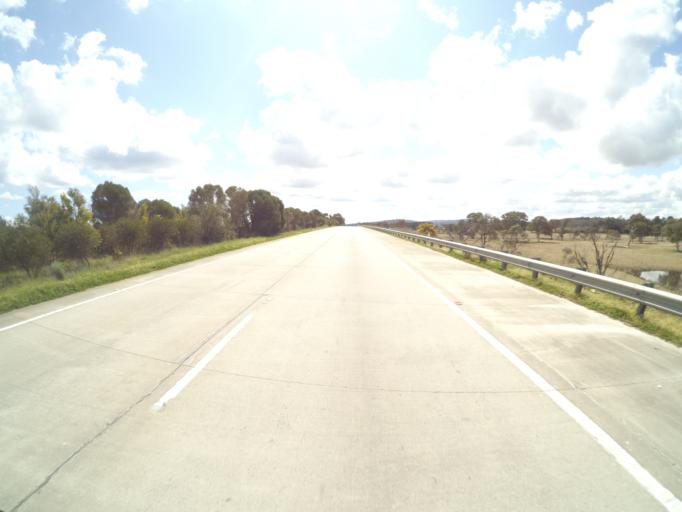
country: AU
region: New South Wales
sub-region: Wingecarribee
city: Moss Vale
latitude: -34.5003
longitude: 150.3105
